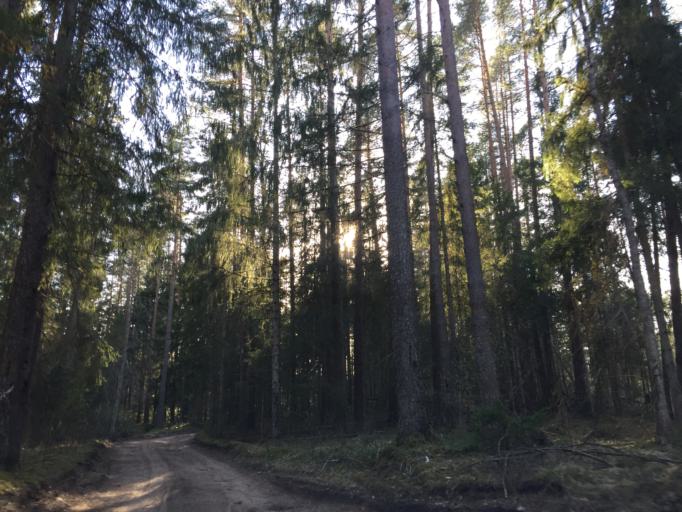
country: LV
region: Valkas Rajons
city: Valka
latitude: 57.7974
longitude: 25.9621
